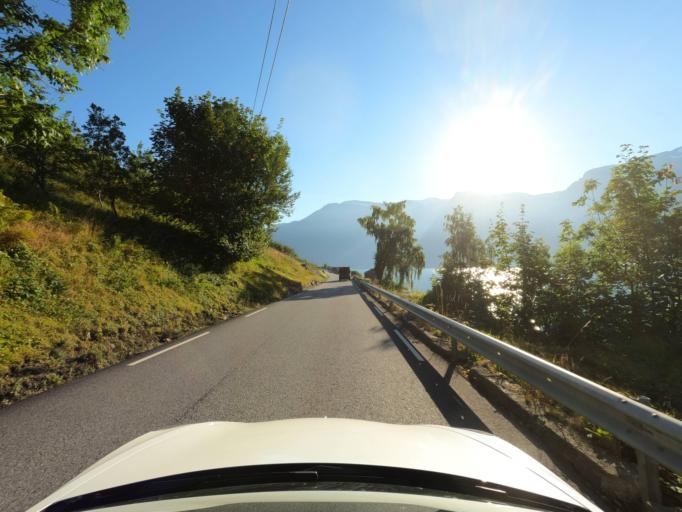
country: NO
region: Hordaland
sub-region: Ullensvang
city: Kinsarvik
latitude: 60.2558
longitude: 6.6201
